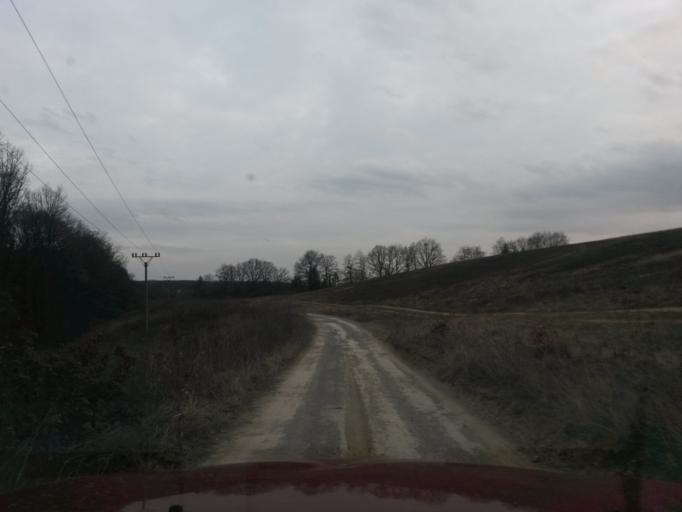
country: SK
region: Kosicky
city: Kosice
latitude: 48.7101
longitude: 21.2926
